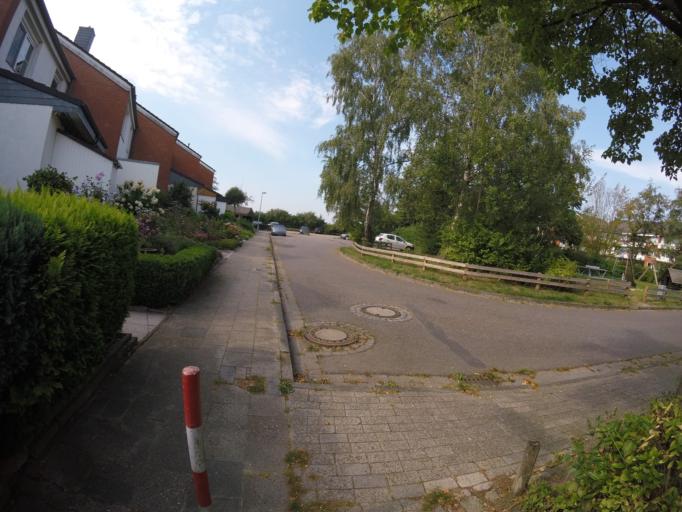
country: DE
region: Lower Saxony
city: Stade
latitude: 53.6120
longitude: 9.4683
